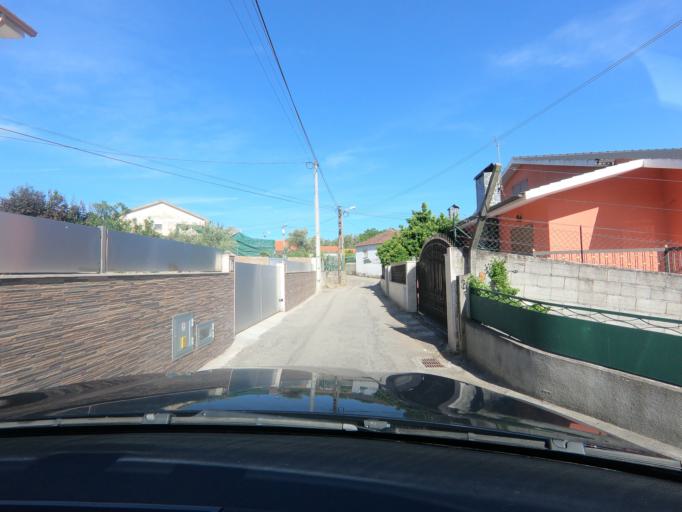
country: PT
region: Vila Real
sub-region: Vila Real
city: Vila Real
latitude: 41.2829
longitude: -7.7013
